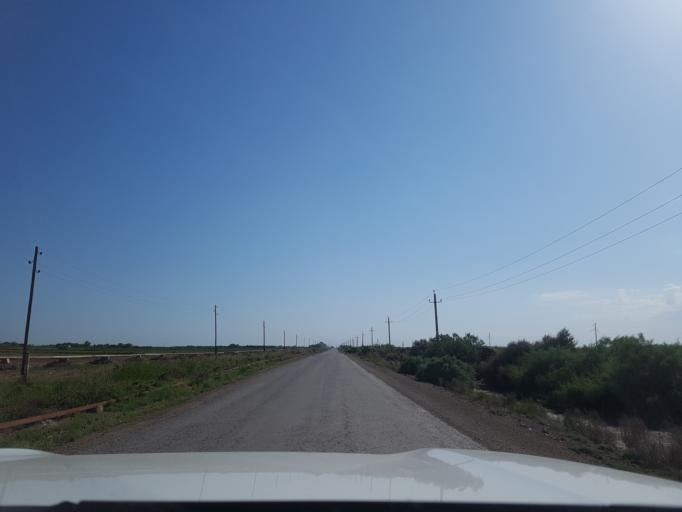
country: TM
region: Dasoguz
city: Koeneuergench
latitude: 42.0914
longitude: 58.8890
